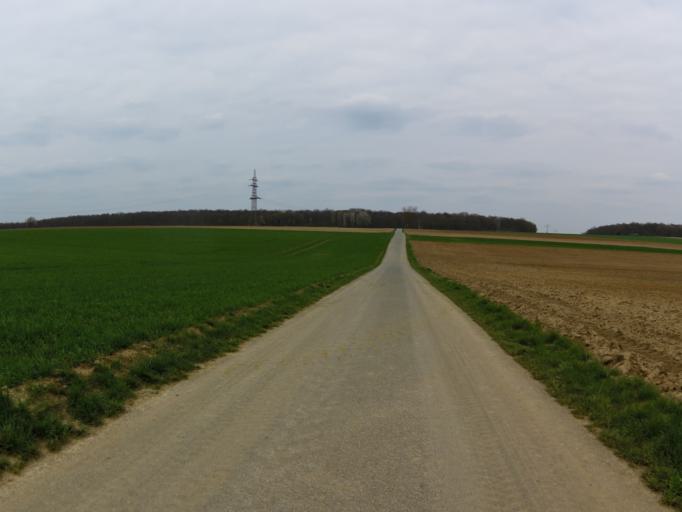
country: DE
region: Bavaria
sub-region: Regierungsbezirk Unterfranken
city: Rottendorf
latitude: 49.8034
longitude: 10.0282
